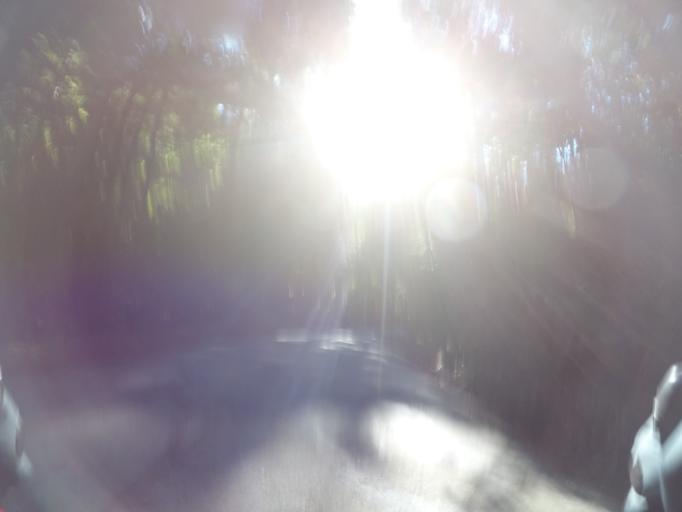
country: US
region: California
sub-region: Santa Clara County
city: Lexington Hills
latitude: 37.1464
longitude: -122.0195
